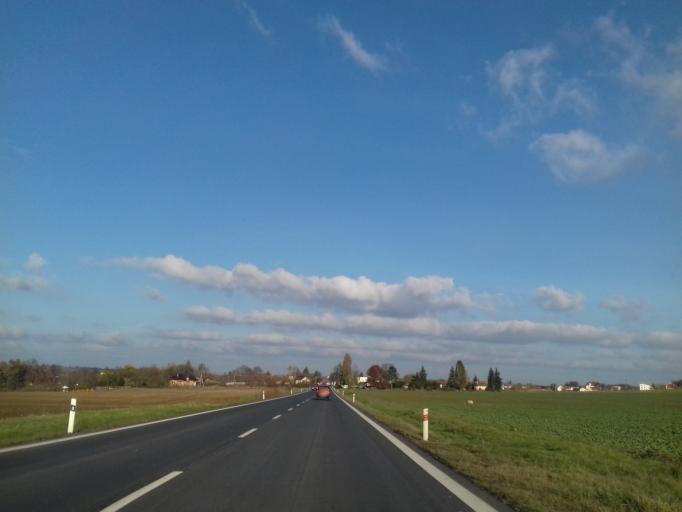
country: CZ
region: Plzensky
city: Stod
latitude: 49.6290
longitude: 13.1544
